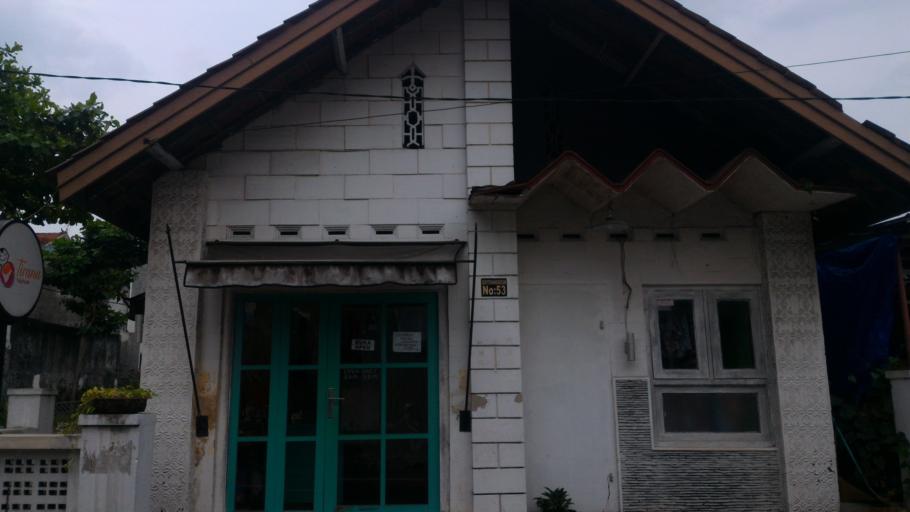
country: ID
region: Daerah Istimewa Yogyakarta
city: Kasihan
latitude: -7.8176
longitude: 110.3576
